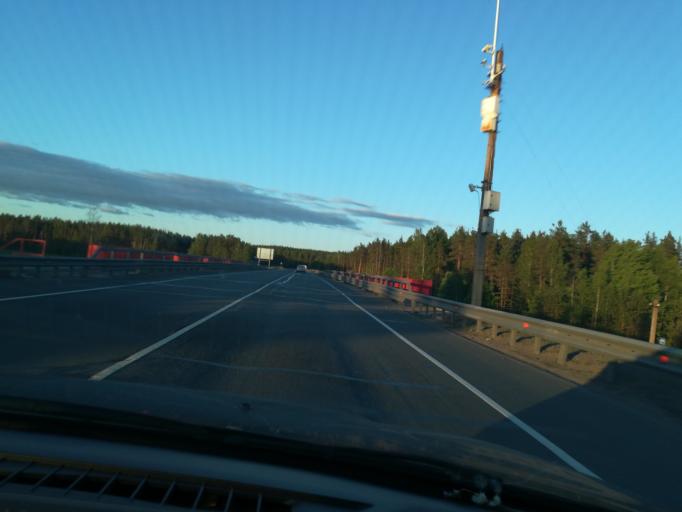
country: RU
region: Leningrad
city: Yakovlevo
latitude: 60.3602
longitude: 29.5339
